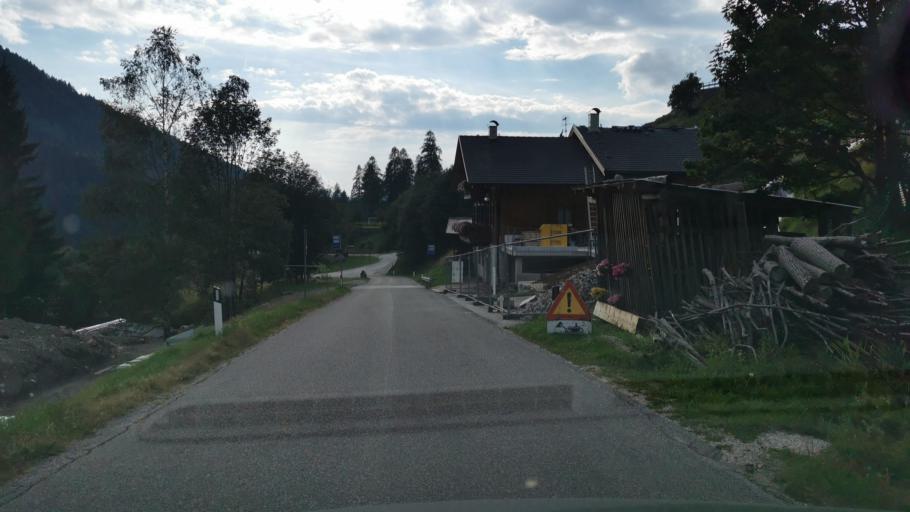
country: IT
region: Trentino-Alto Adige
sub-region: Provincia di Trento
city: Palu del Fersina
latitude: 46.1295
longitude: 11.3559
